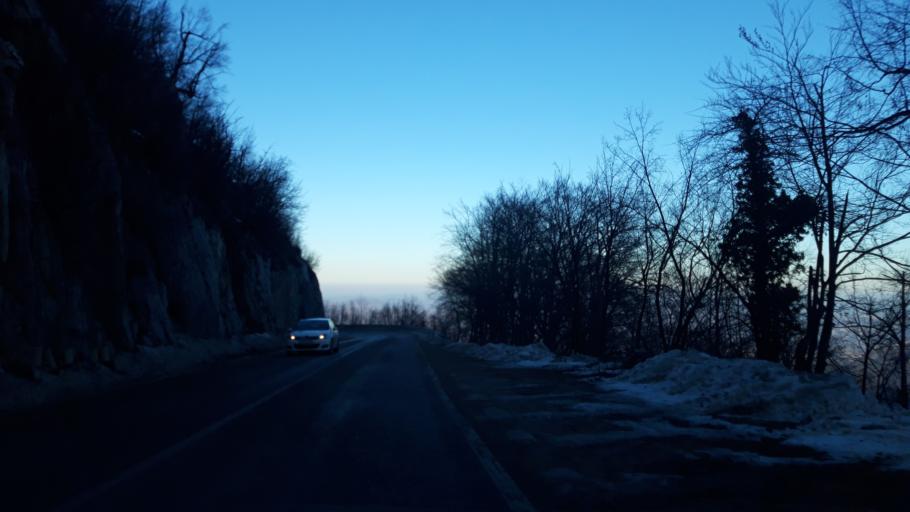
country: BA
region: Republika Srpska
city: Vlasenica
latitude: 44.1530
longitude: 18.9430
